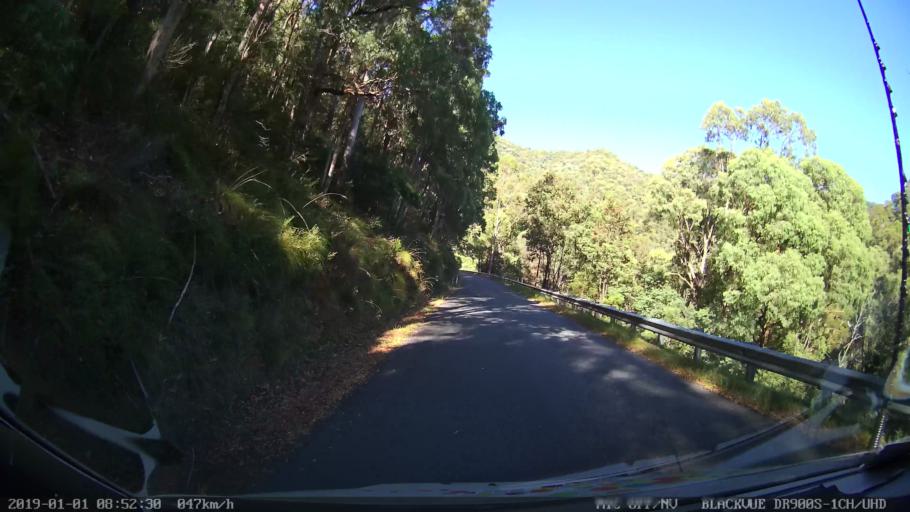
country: AU
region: New South Wales
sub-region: Snowy River
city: Jindabyne
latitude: -36.2678
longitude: 148.1962
